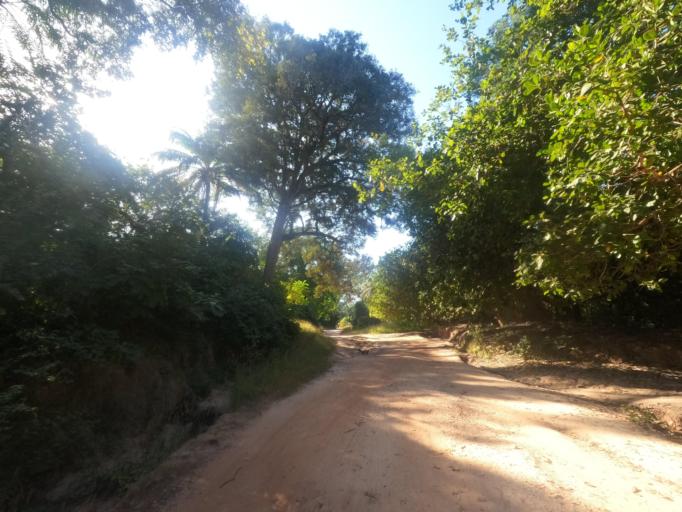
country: GW
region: Cacheu
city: Cacheu
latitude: 12.3938
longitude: -16.2268
